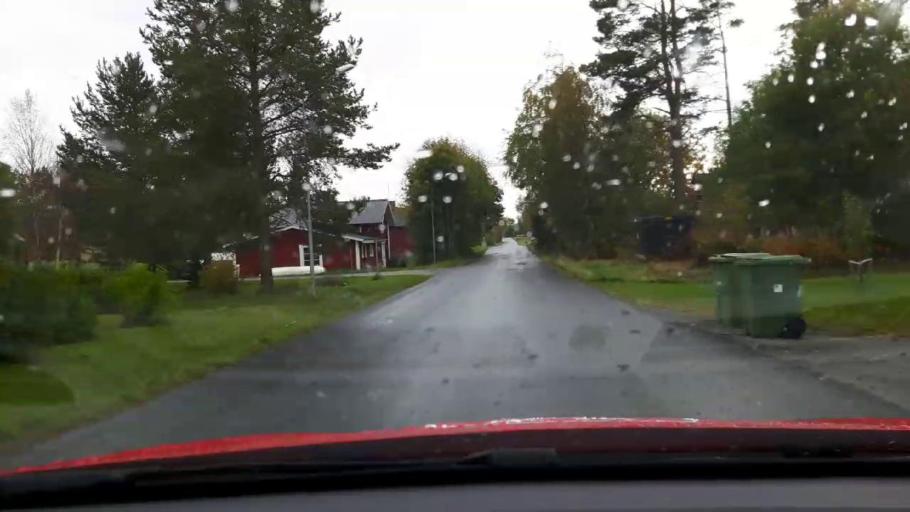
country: SE
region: Jaemtland
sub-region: Bergs Kommun
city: Hoverberg
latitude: 62.9274
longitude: 14.5160
